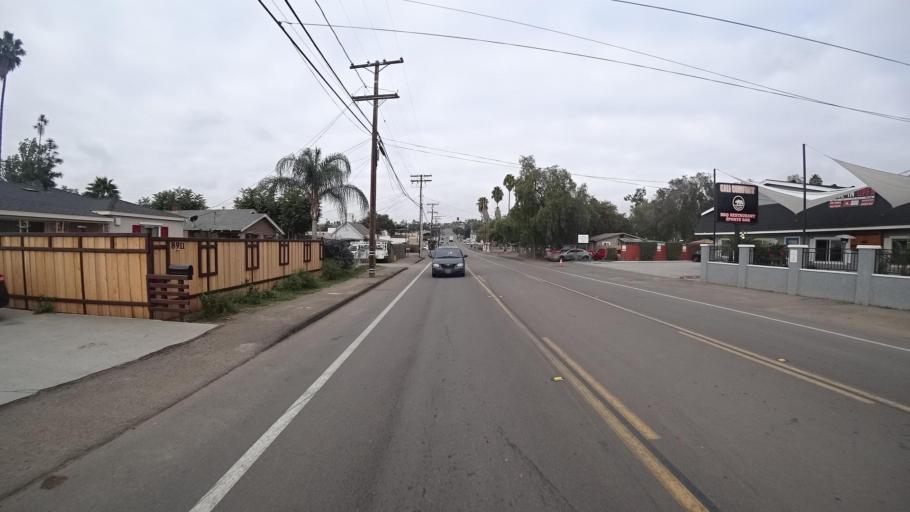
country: US
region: California
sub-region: San Diego County
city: Spring Valley
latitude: 32.7366
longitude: -117.0077
